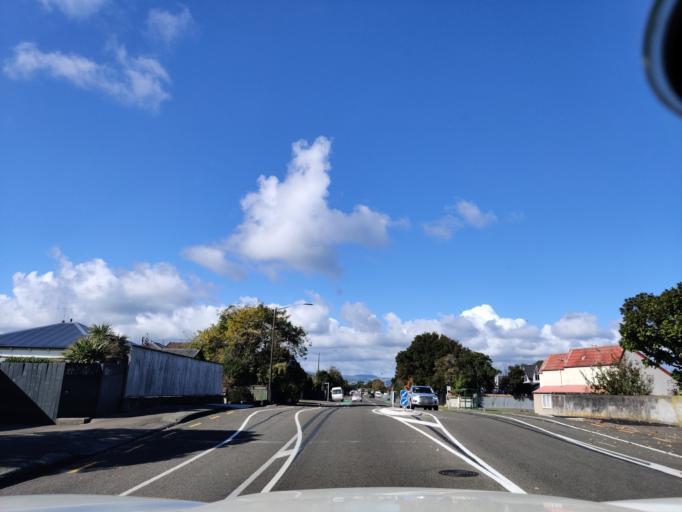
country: NZ
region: Manawatu-Wanganui
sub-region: Palmerston North City
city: Palmerston North
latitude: -40.3494
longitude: 175.5970
